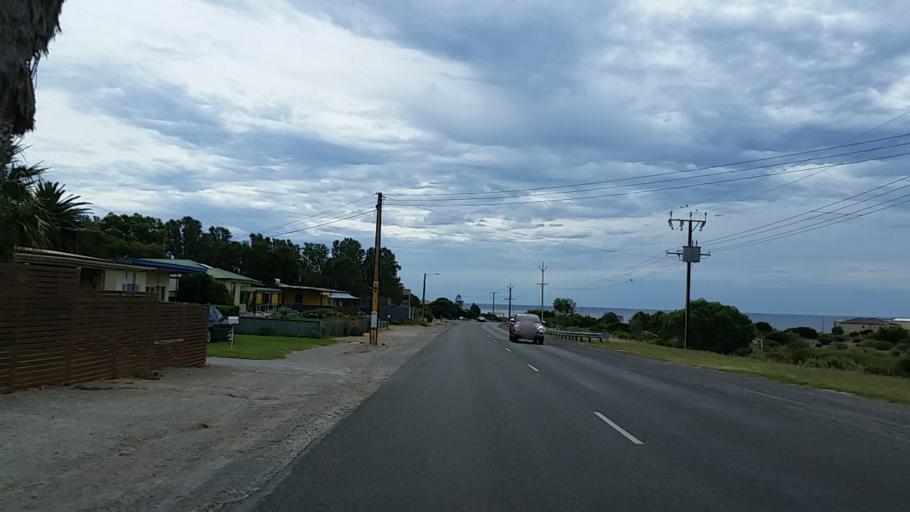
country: AU
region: South Australia
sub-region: Onkaparinga
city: Port Willunga
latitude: -35.3295
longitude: 138.4526
